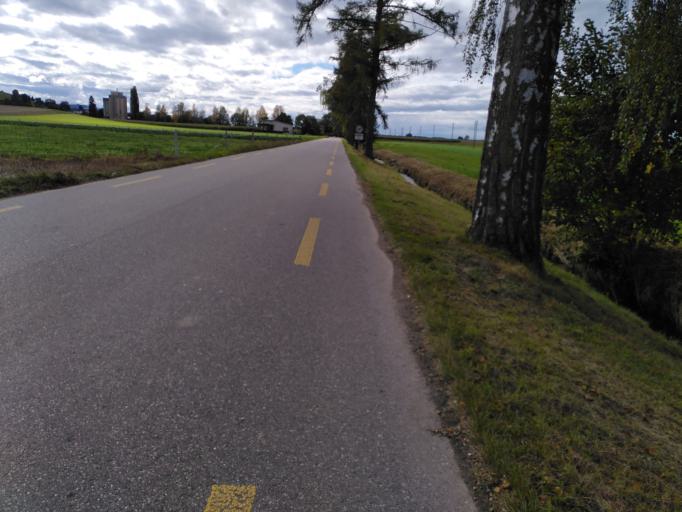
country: CH
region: Bern
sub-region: Emmental District
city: Ersigen
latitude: 47.1078
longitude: 7.6075
